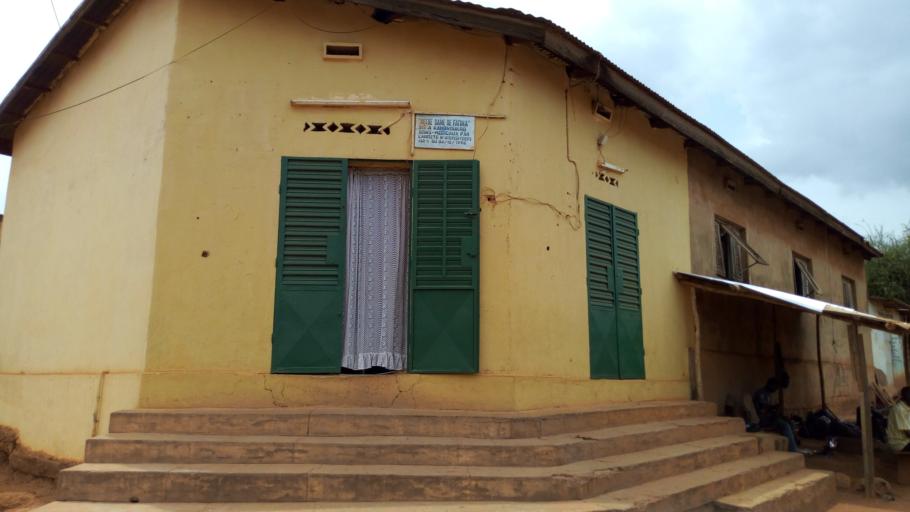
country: CI
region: Vallee du Bandama
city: Bouake
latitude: 7.6997
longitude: -5.0286
